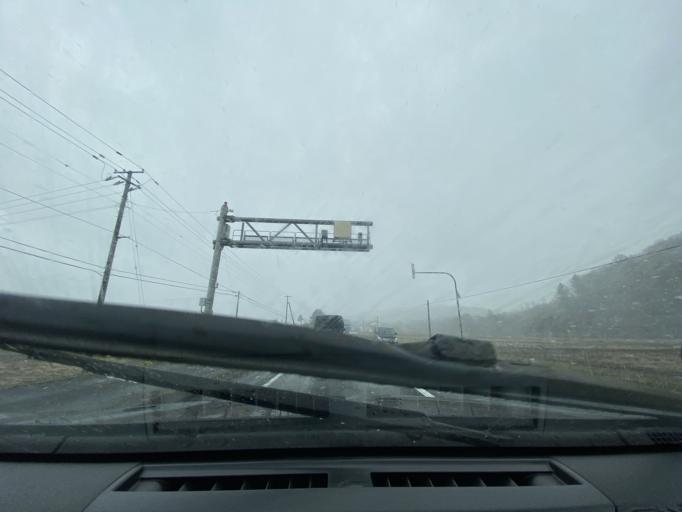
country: JP
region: Hokkaido
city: Fukagawa
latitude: 43.7096
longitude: 142.1338
